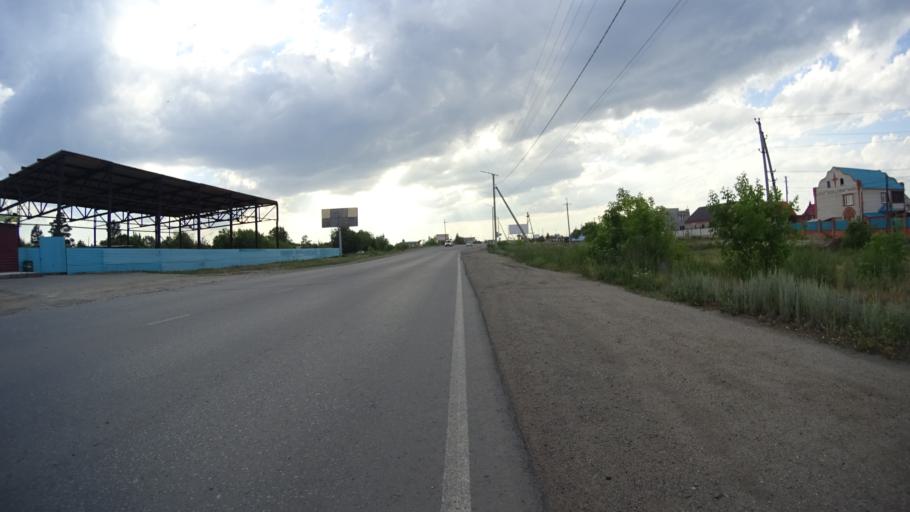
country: RU
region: Chelyabinsk
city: Troitsk
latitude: 54.0842
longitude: 61.5066
